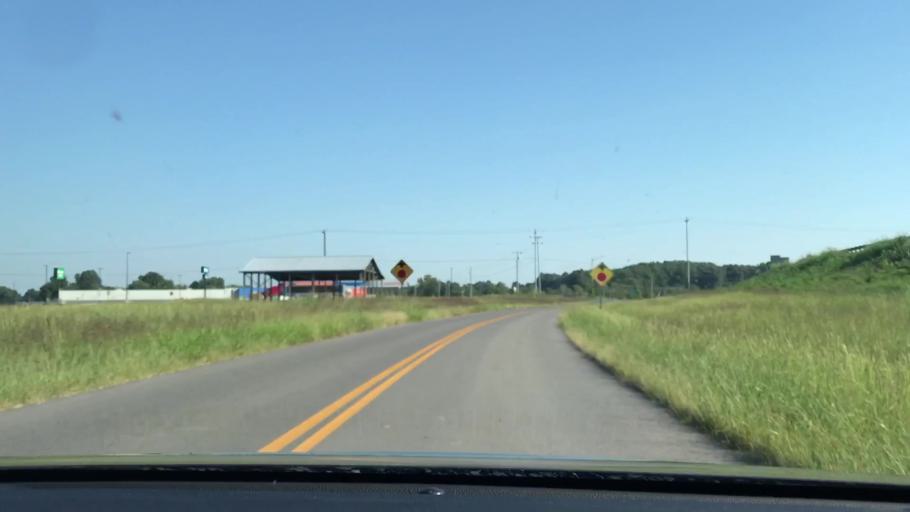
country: US
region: Kentucky
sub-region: Fulton County
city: Fulton
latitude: 36.5138
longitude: -88.8999
